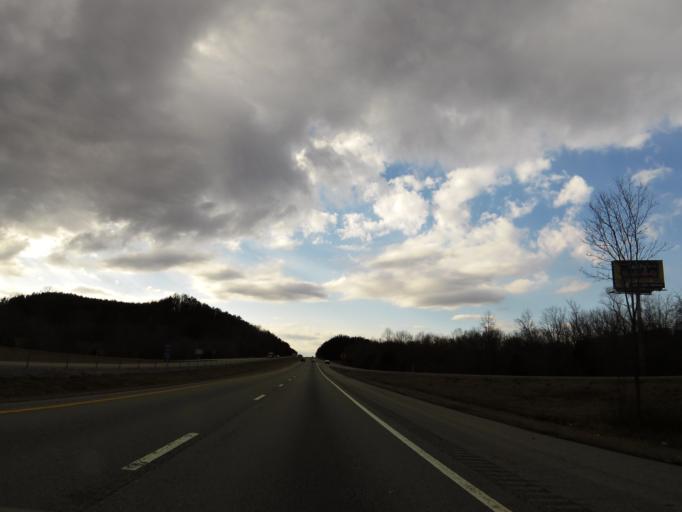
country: US
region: Tennessee
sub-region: Cumberland County
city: Fairfield Glade
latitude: 35.9069
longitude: -84.8774
